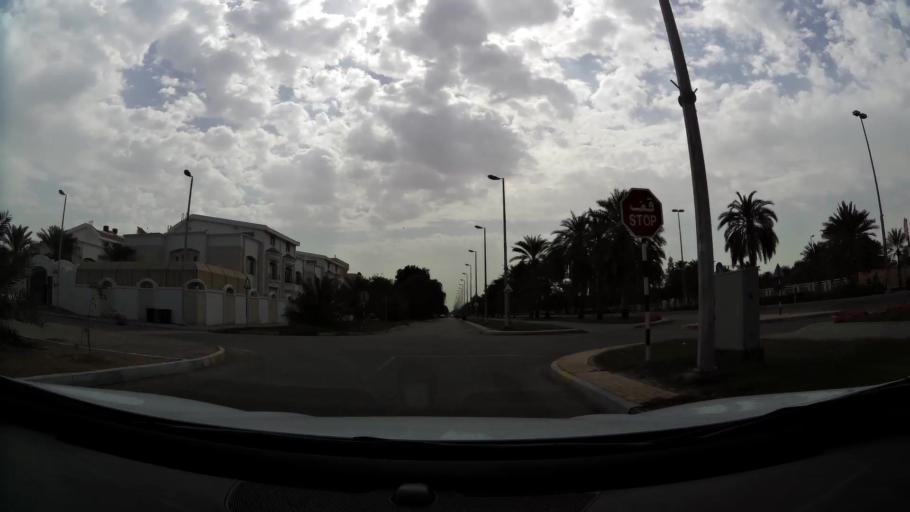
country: AE
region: Abu Dhabi
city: Abu Dhabi
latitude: 24.4420
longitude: 54.3643
